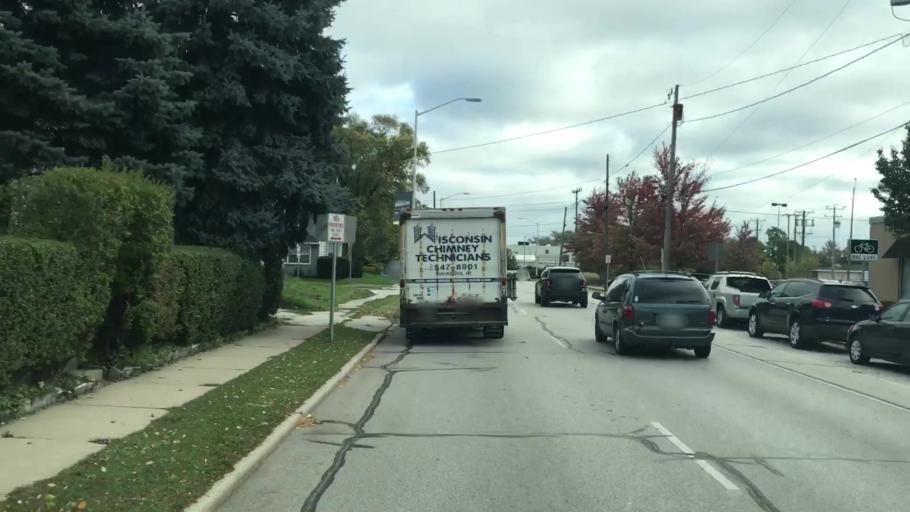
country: US
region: Wisconsin
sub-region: Waukesha County
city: Waukesha
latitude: 43.0151
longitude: -88.2309
